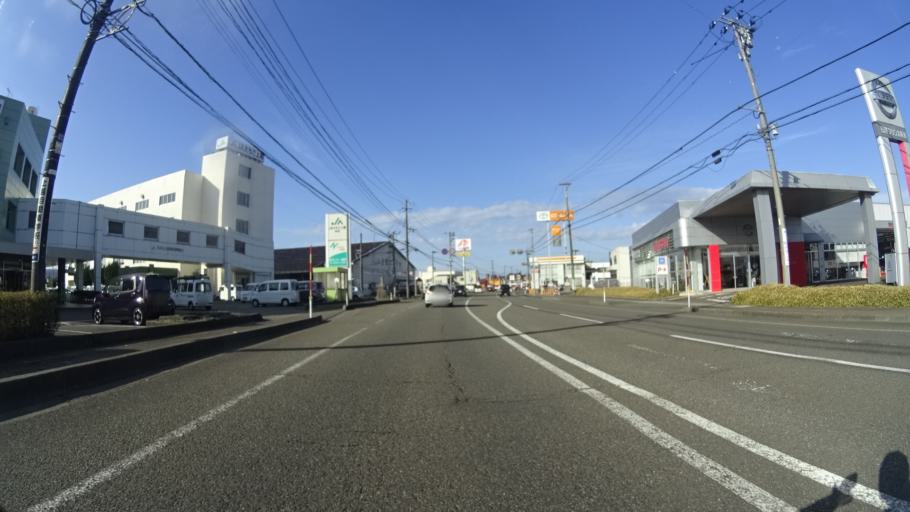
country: JP
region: Niigata
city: Joetsu
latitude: 37.1356
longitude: 138.2418
